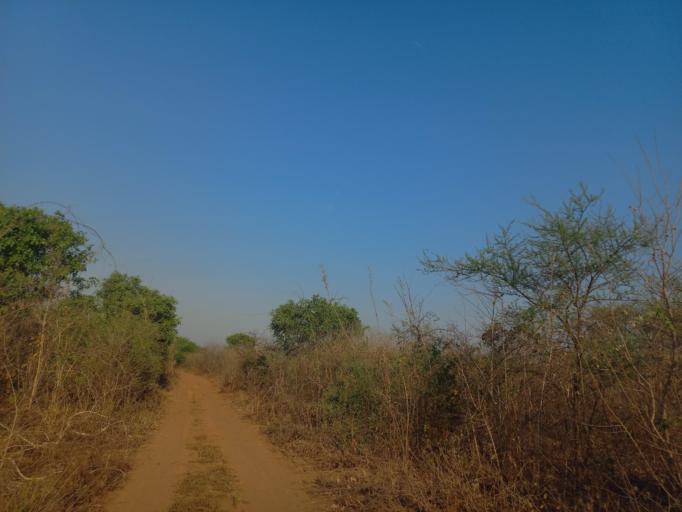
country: ZM
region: Lusaka
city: Luangwa
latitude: -15.4213
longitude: 30.2681
